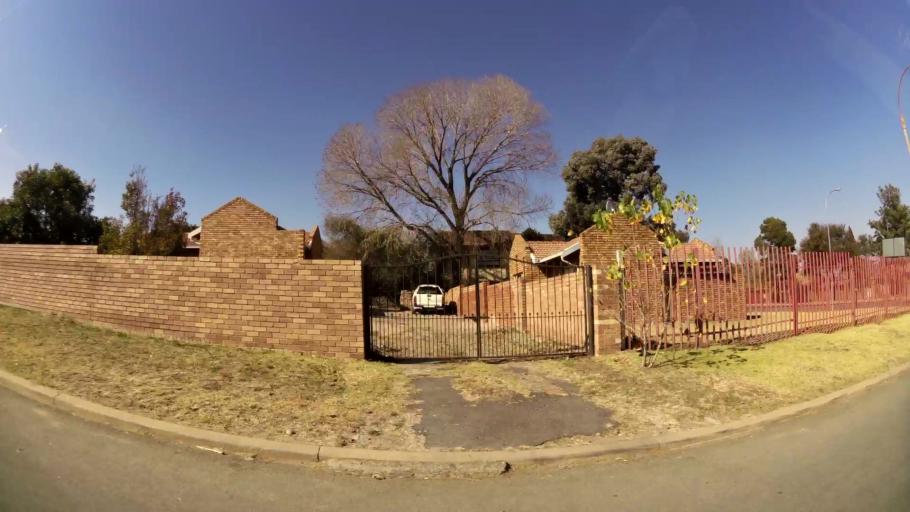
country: ZA
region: Gauteng
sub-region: Ekurhuleni Metropolitan Municipality
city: Tembisa
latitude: -26.0354
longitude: 28.2345
